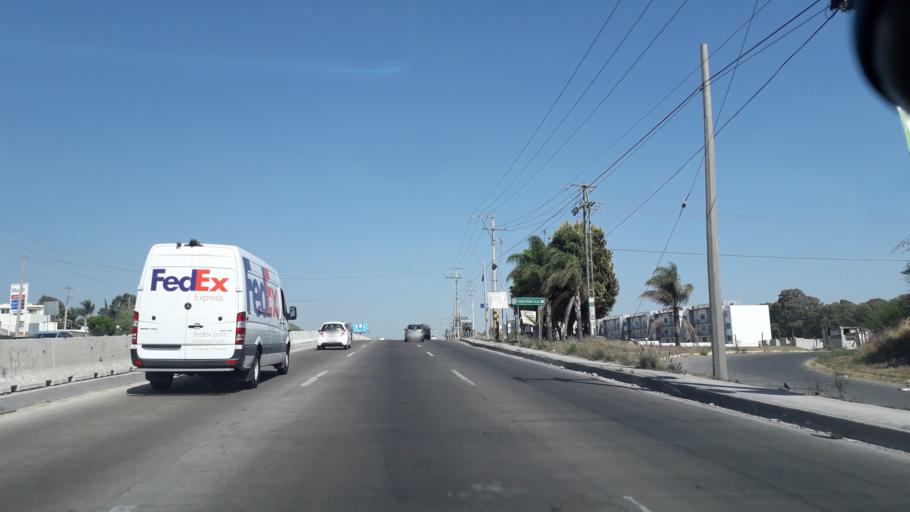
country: MX
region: Puebla
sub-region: Puebla
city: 18 de Marzo
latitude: 18.9719
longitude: -98.2045
